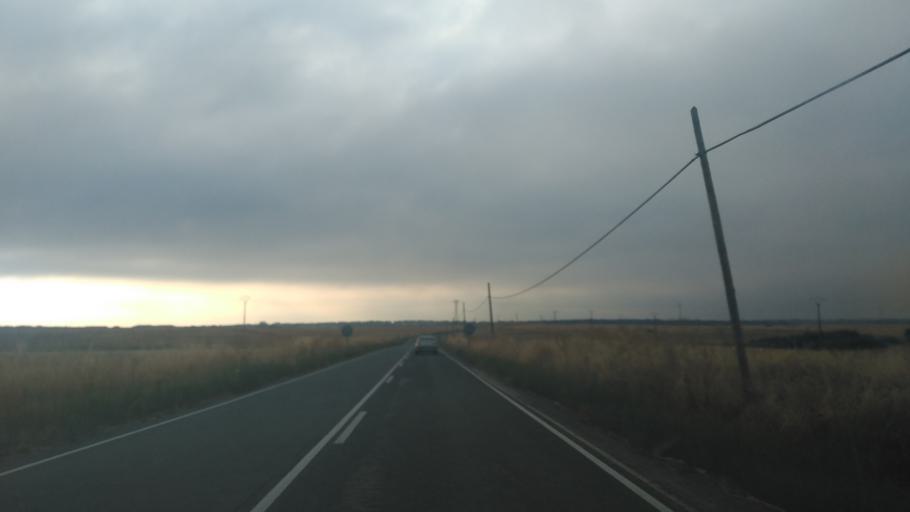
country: ES
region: Castille and Leon
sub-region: Provincia de Salamanca
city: Robliza de Cojos
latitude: 40.8654
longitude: -5.9715
